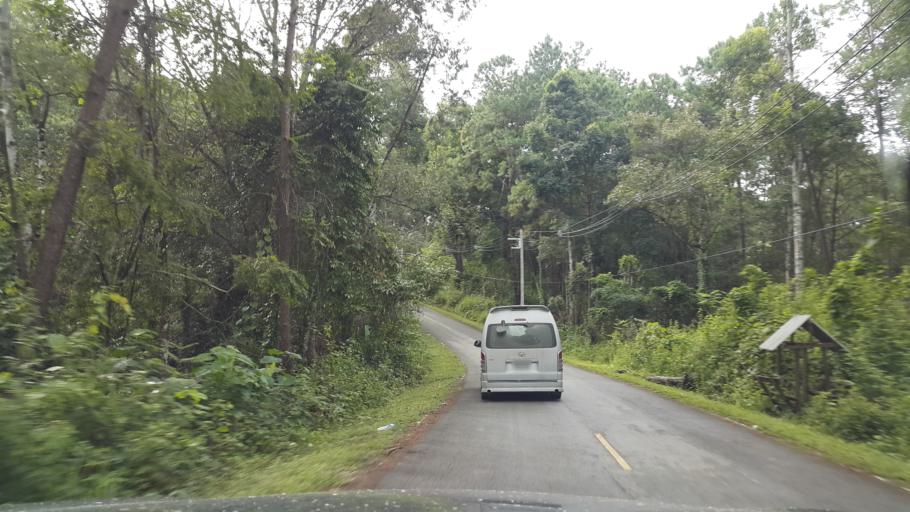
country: TH
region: Chiang Mai
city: Chaem Luang
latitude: 18.9328
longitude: 98.4705
